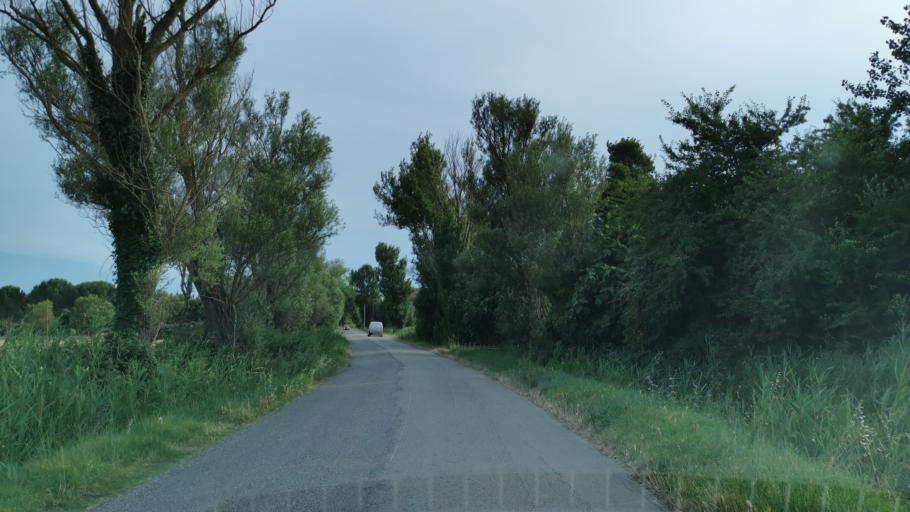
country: FR
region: Languedoc-Roussillon
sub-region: Departement de l'Aude
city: Narbonne
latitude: 43.2009
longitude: 2.9976
